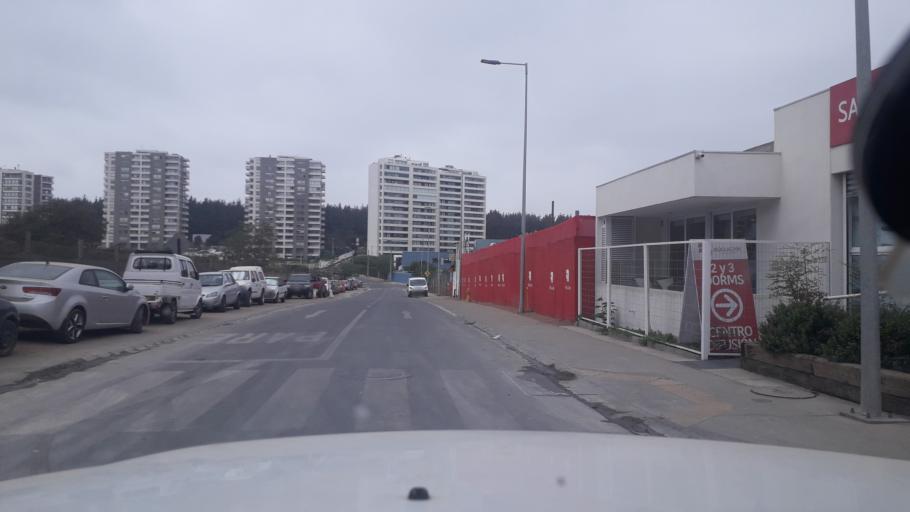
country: CL
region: Valparaiso
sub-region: Provincia de Valparaiso
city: Vina del Mar
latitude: -32.9571
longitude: -71.5428
